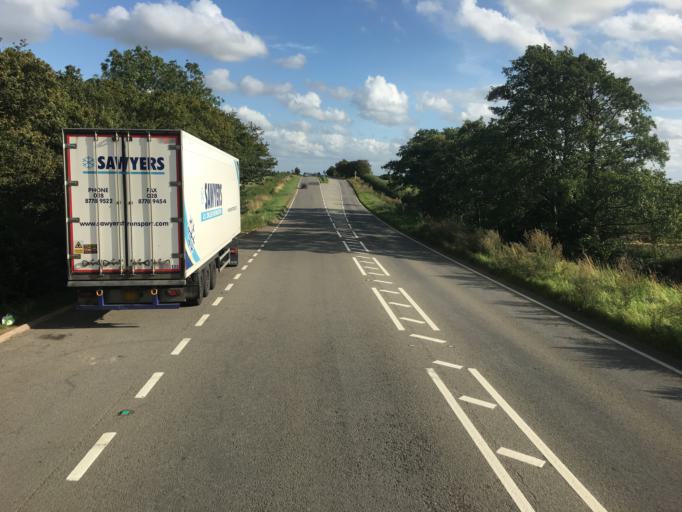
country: GB
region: England
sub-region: Leicestershire
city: Lutterworth
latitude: 52.4477
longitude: -1.2499
